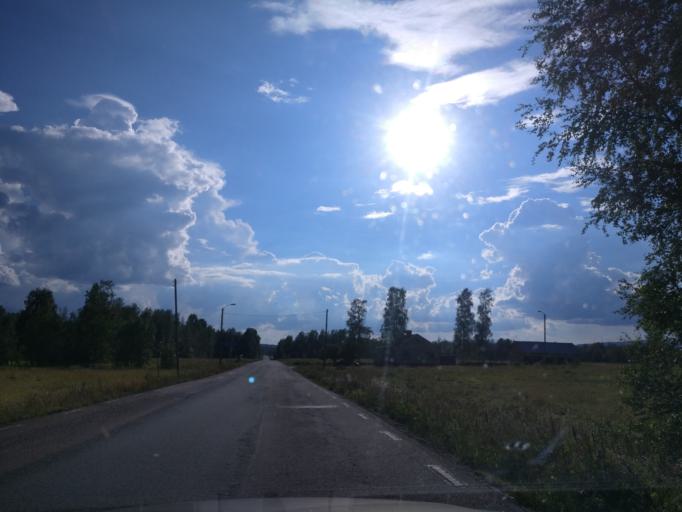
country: SE
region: Dalarna
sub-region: Ludvika Kommun
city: Grangesberg
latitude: 60.2676
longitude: 15.0071
